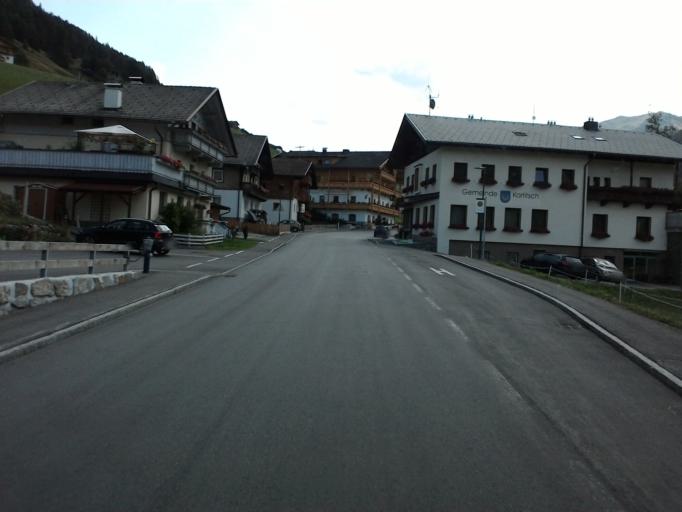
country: AT
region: Tyrol
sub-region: Politischer Bezirk Lienz
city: Kartitsch
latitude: 46.7262
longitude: 12.4979
